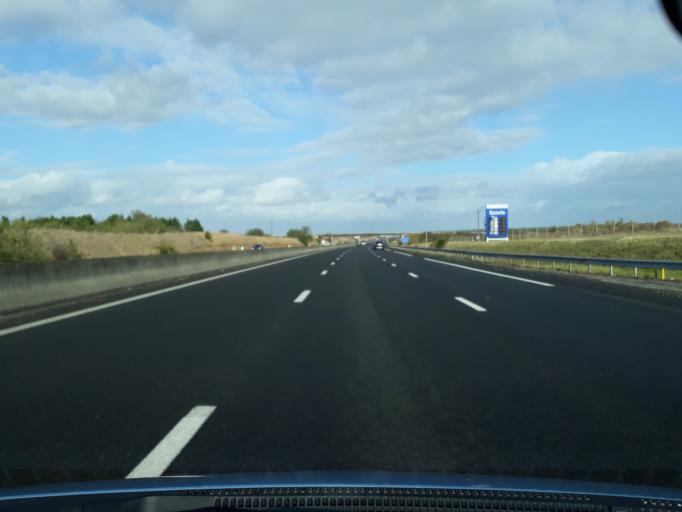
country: FR
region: Centre
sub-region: Departement du Loir-et-Cher
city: La Chaussee-Saint-Victor
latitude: 47.6442
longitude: 1.3651
